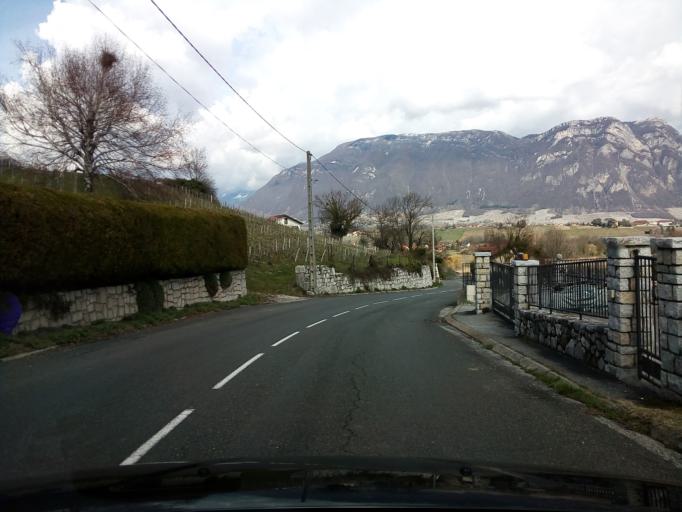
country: FR
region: Rhone-Alpes
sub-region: Departement de la Savoie
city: Les Marches
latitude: 45.4922
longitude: 5.9816
